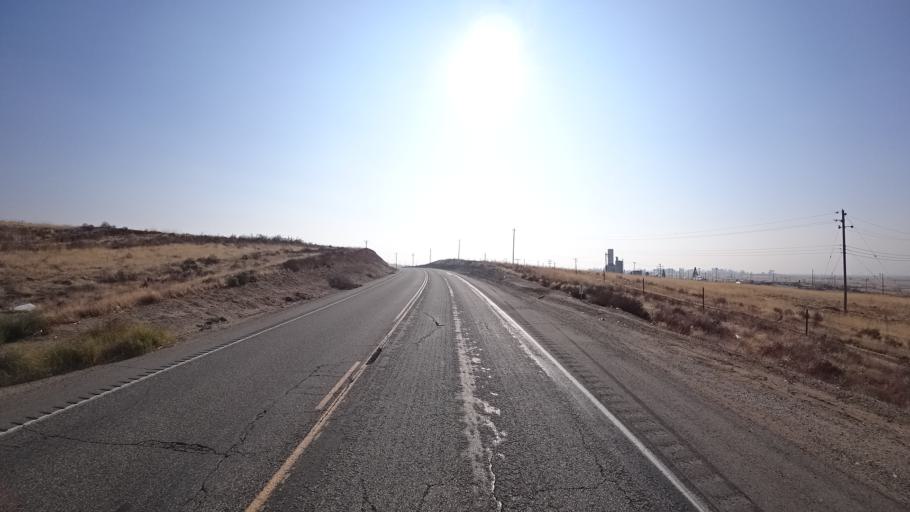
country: US
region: California
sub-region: Kern County
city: Lamont
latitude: 35.3800
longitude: -118.8502
